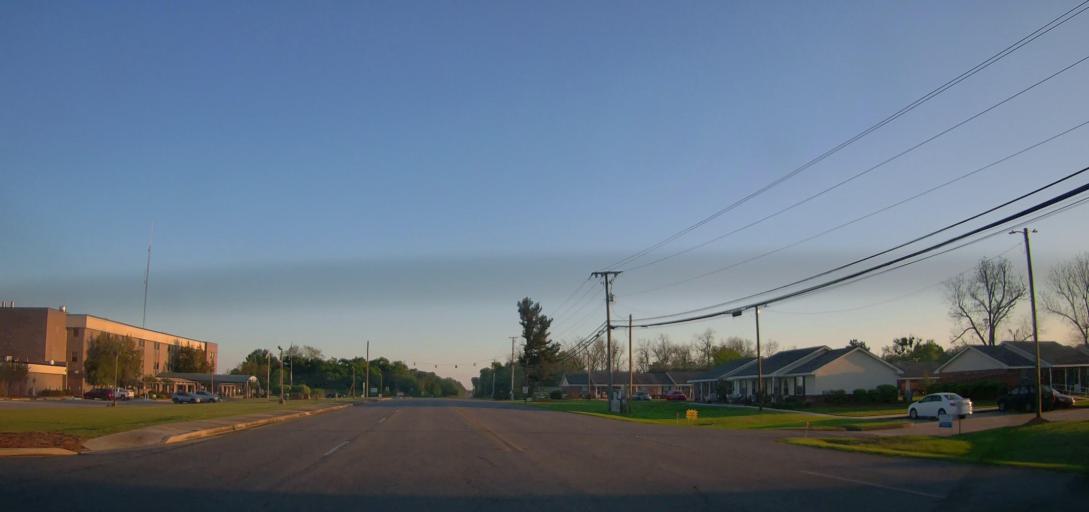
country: US
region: Georgia
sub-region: Ben Hill County
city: Fitzgerald
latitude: 31.6985
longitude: -83.2610
